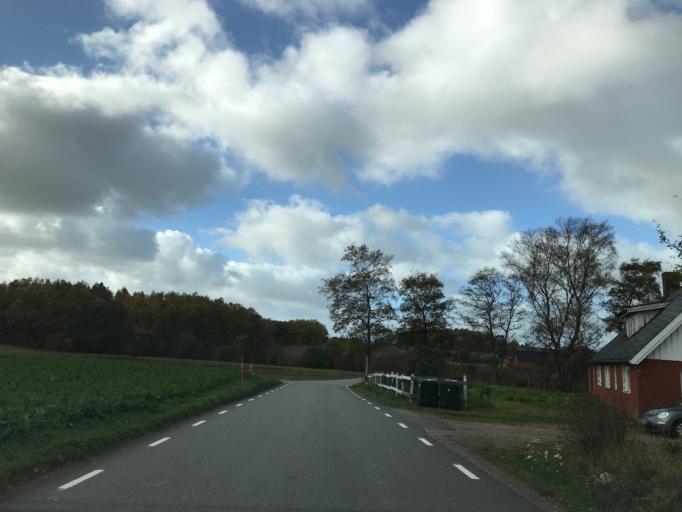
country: SE
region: Skane
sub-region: Bjuvs Kommun
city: Billesholm
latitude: 56.0115
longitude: 12.9866
